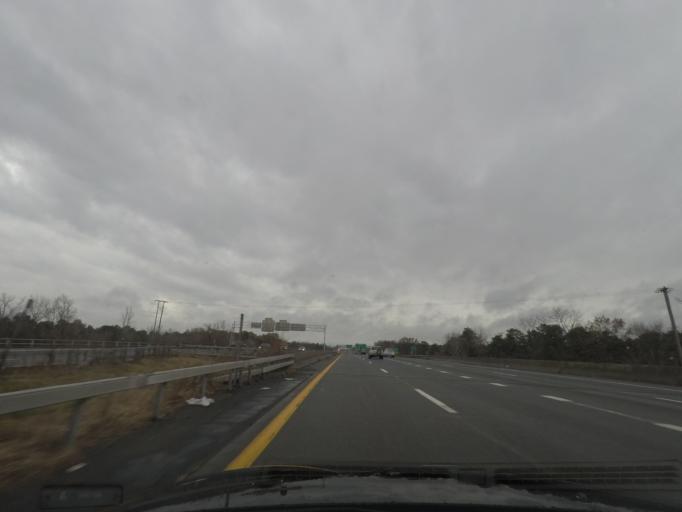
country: US
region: New York
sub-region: Albany County
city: Colonie
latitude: 42.7029
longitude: -73.8340
